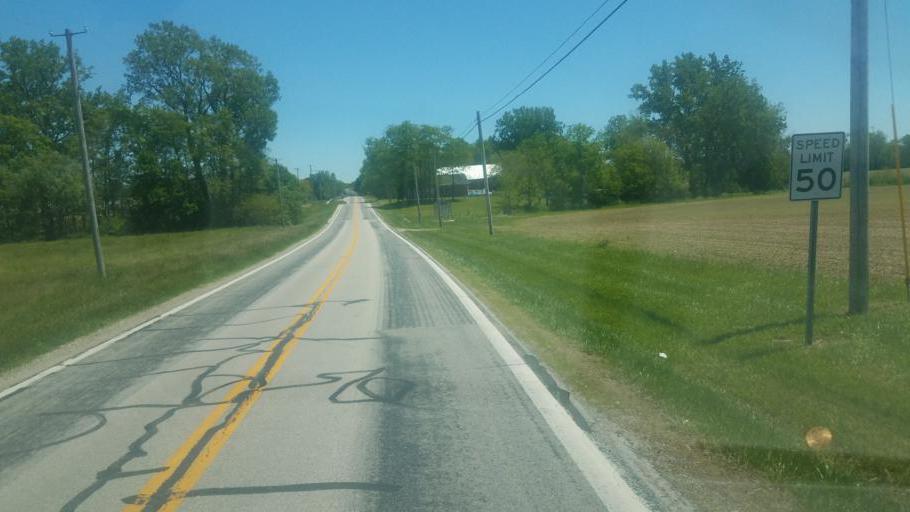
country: US
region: Ohio
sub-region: Darke County
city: Versailles
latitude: 40.2323
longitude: -84.5014
